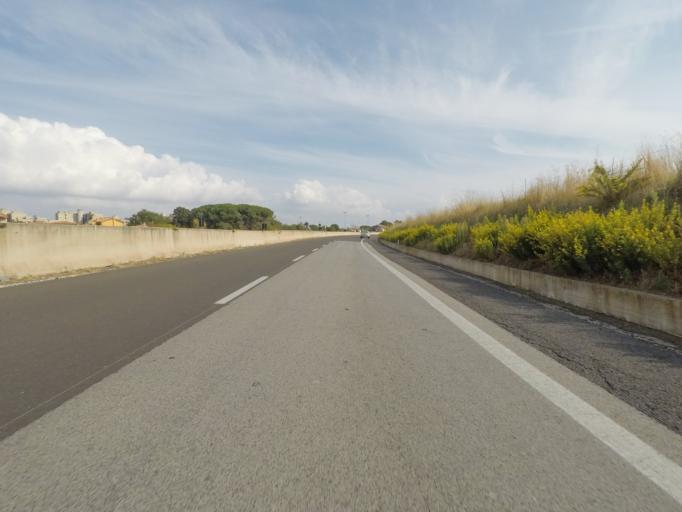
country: IT
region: Latium
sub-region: Provincia di Viterbo
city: Montalto di Castro
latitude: 42.3459
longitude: 11.6120
